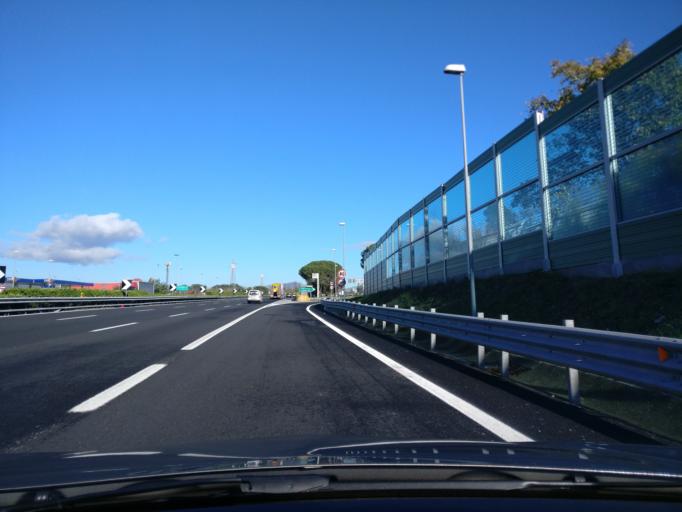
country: IT
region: Campania
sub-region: Provincia di Caserta
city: Teano
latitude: 41.2314
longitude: 14.0939
